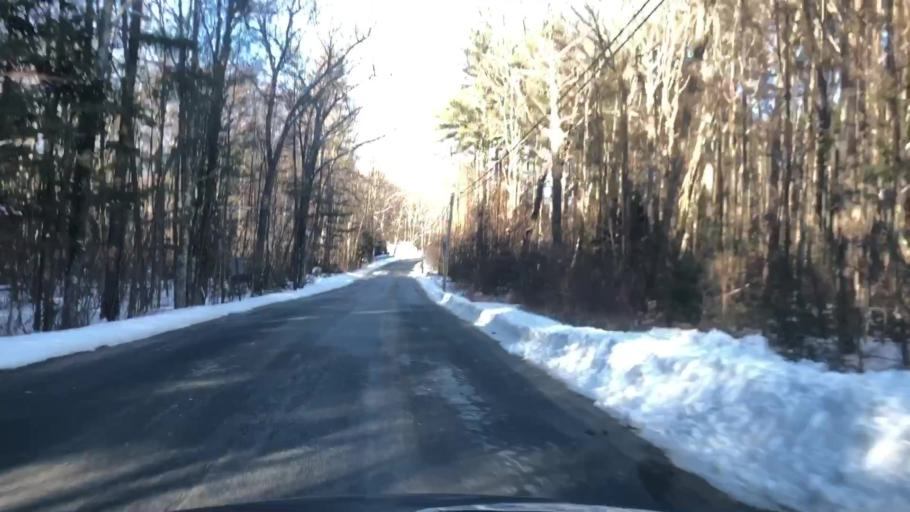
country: US
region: New Hampshire
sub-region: Hillsborough County
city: Wilton
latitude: 42.8094
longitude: -71.7052
